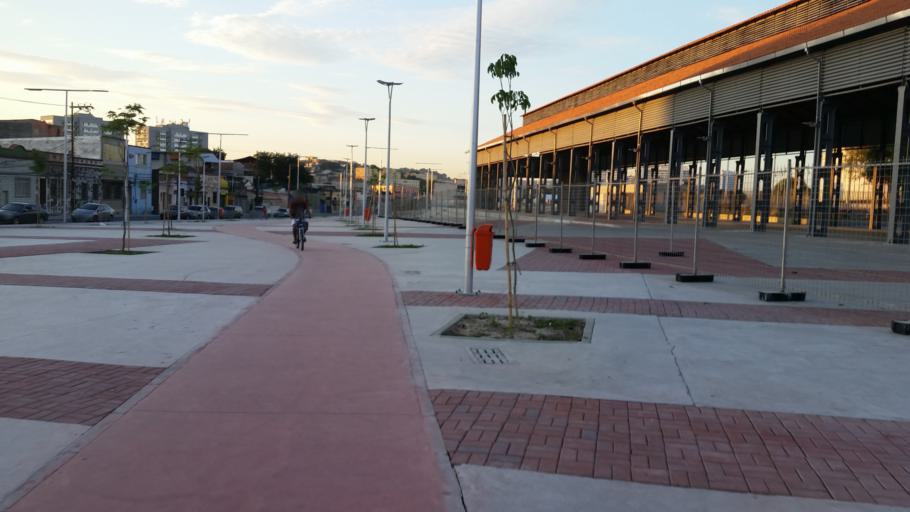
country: BR
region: Rio de Janeiro
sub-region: Rio De Janeiro
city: Rio de Janeiro
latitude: -22.8941
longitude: -43.2951
